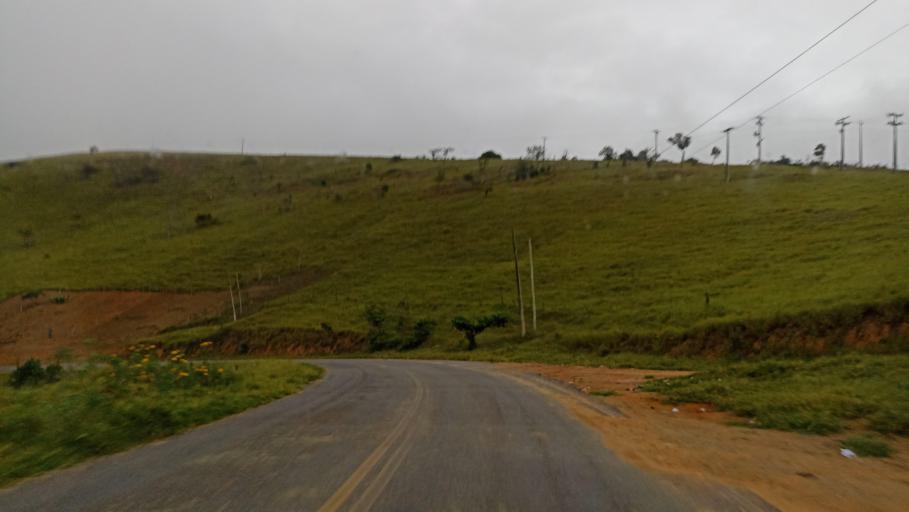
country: BR
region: Bahia
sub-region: Itanhem
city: Itanhem
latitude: -16.7329
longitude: -40.4360
